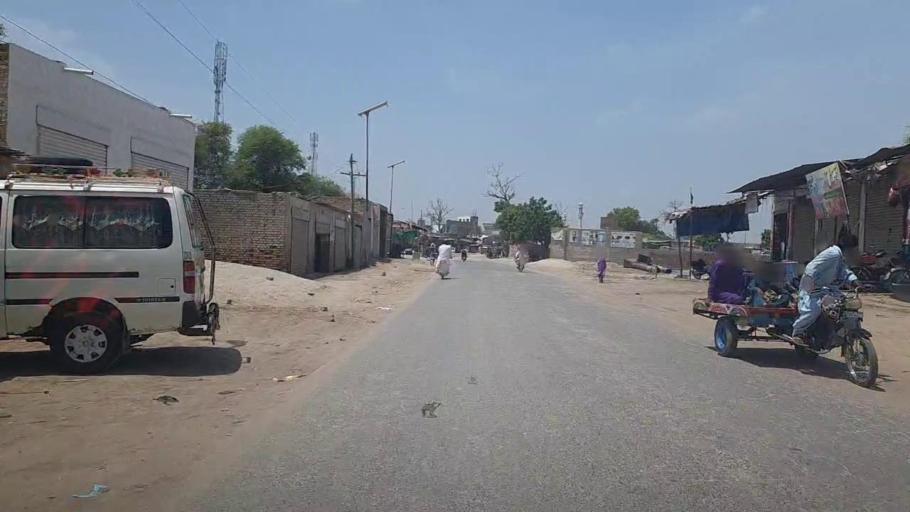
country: PK
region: Sindh
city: Ubauro
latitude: 28.3148
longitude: 69.7947
